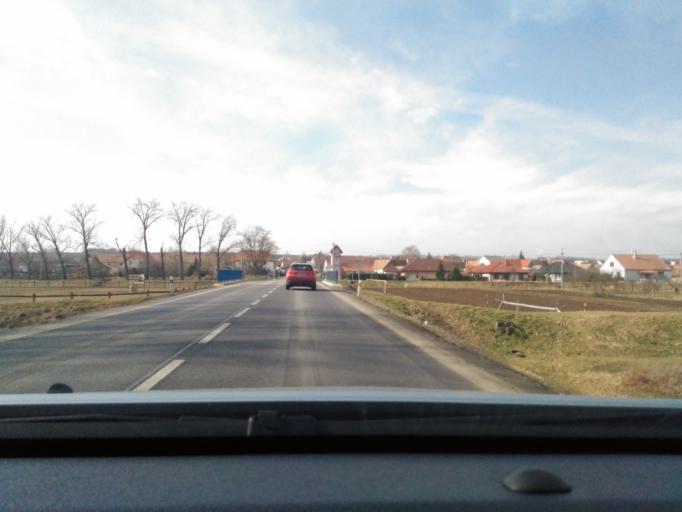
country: CZ
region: South Moravian
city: Bozice
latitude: 48.8739
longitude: 16.2276
